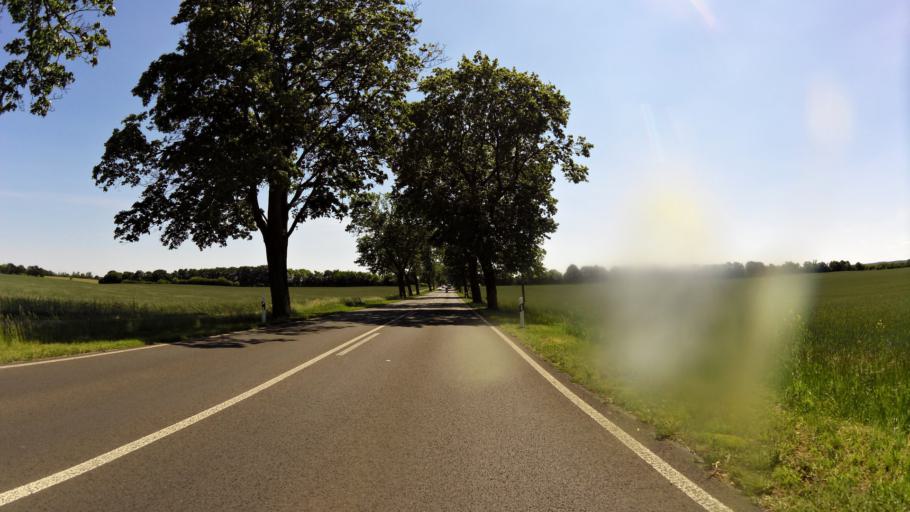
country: DE
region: Brandenburg
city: Lebus
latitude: 52.3951
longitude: 14.5168
